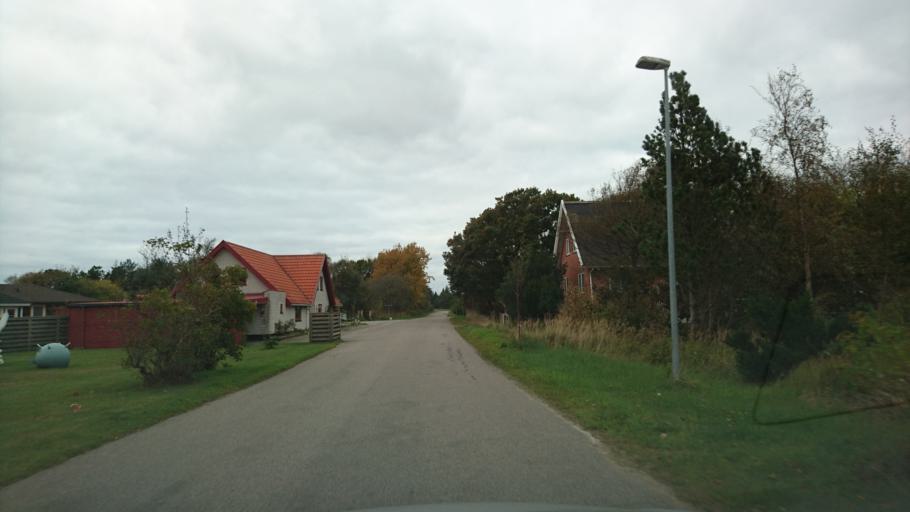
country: DK
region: North Denmark
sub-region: Frederikshavn Kommune
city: Skagen
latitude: 57.6603
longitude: 10.4624
